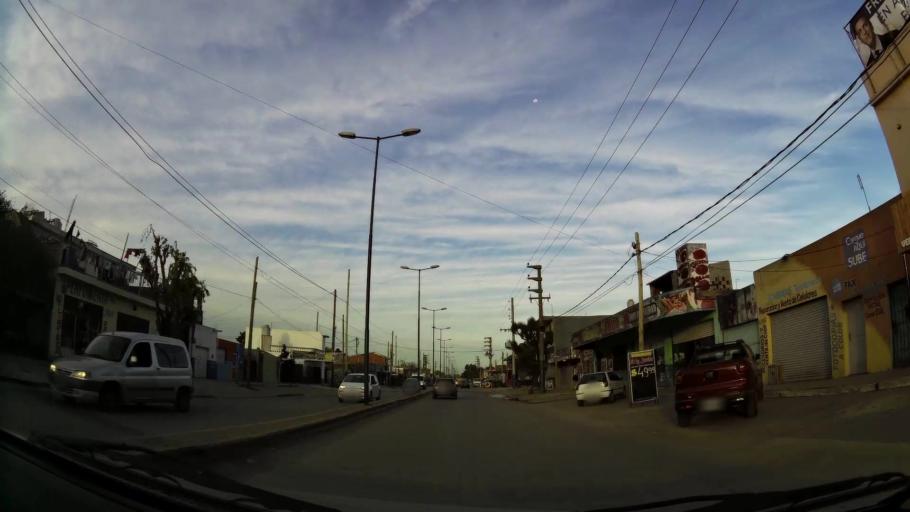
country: AR
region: Buenos Aires
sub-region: Partido de Almirante Brown
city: Adrogue
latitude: -34.7757
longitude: -58.3284
